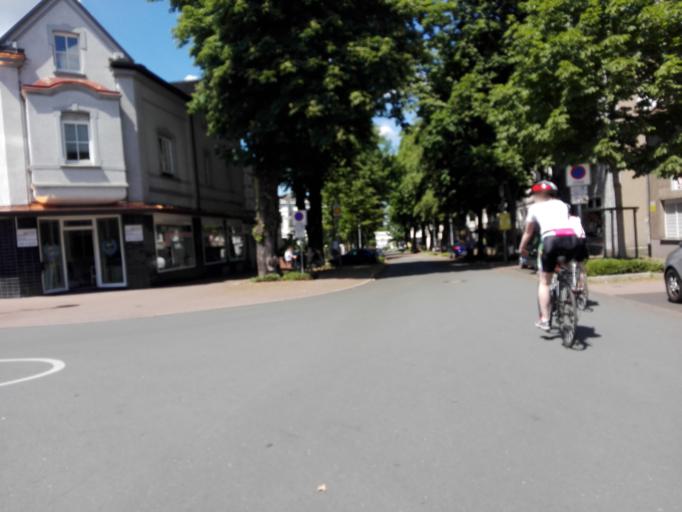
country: DE
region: North Rhine-Westphalia
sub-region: Regierungsbezirk Arnsberg
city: Unna
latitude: 51.5397
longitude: 7.6898
